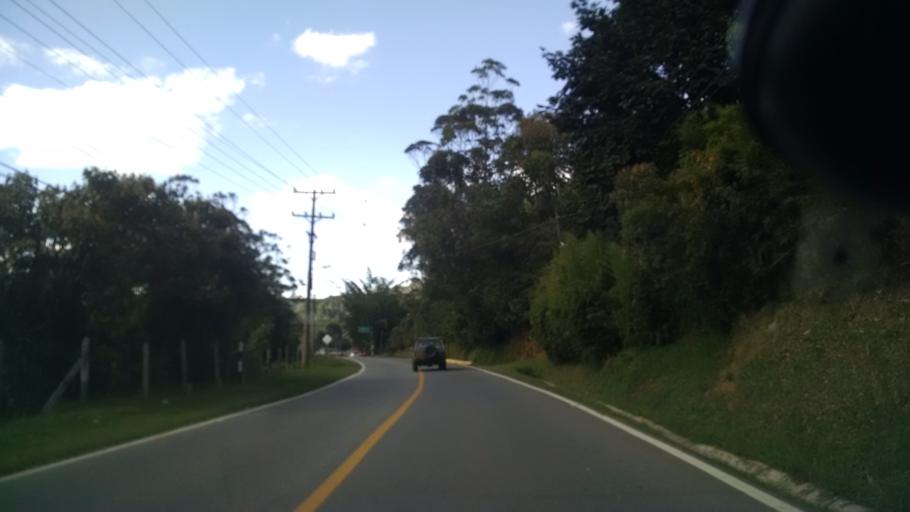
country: CO
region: Antioquia
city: El Retiro
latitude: 6.0916
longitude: -75.4896
